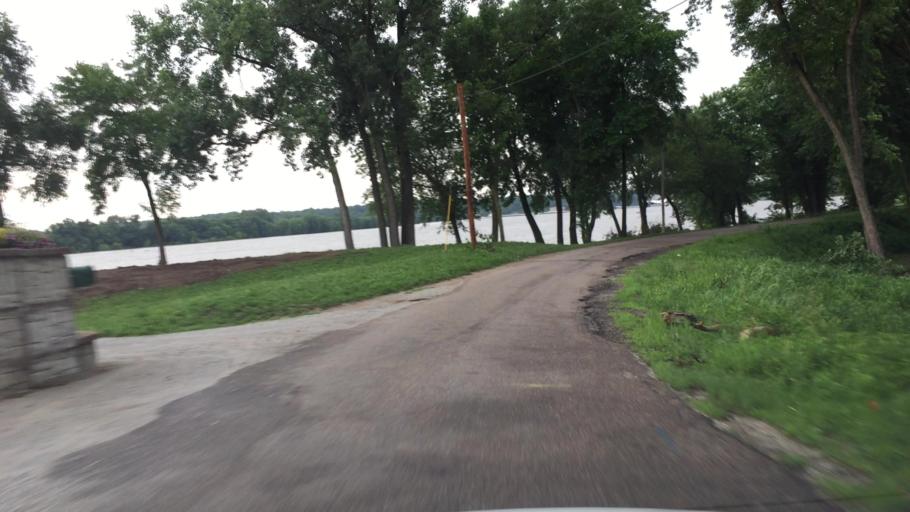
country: US
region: Illinois
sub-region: Hancock County
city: Warsaw
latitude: 40.3654
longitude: -91.4339
